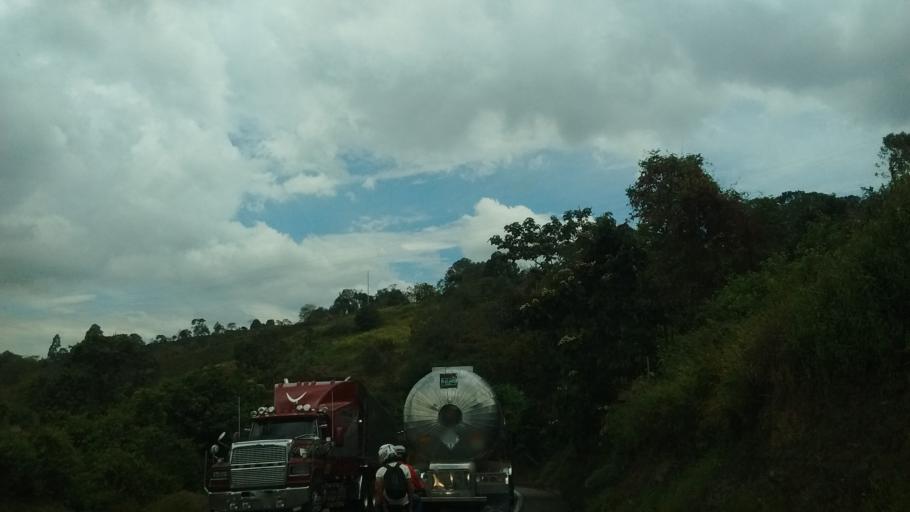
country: CO
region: Cauca
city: Rosas
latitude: 2.3092
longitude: -76.6879
